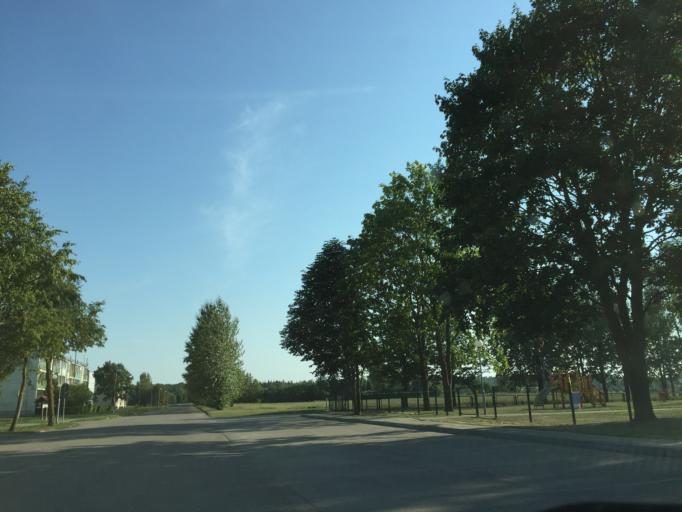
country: LT
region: Siauliu apskritis
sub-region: Joniskis
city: Joniskis
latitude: 56.4190
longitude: 23.6986
